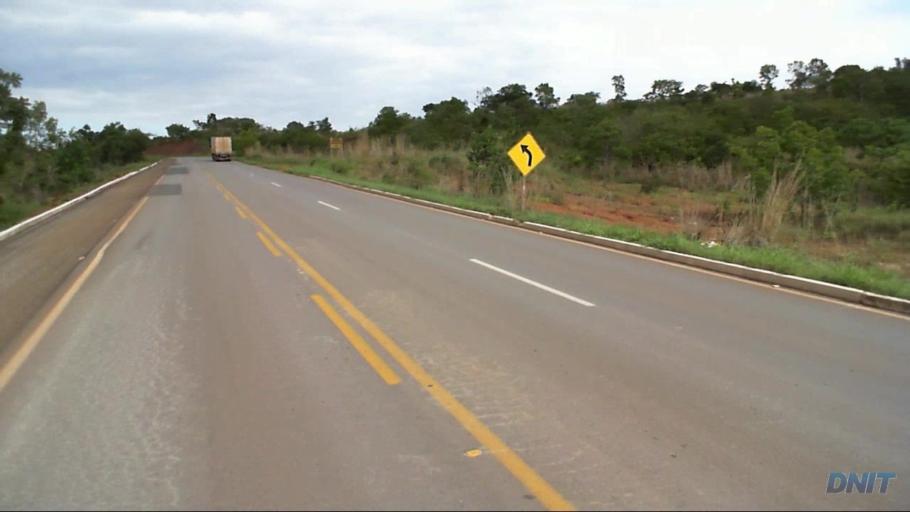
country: BR
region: Goias
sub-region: Barro Alto
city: Barro Alto
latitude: -14.8700
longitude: -49.0066
